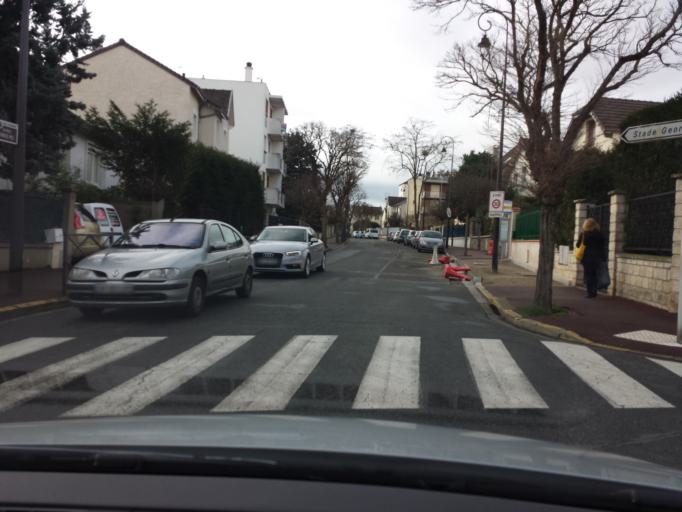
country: FR
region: Ile-de-France
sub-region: Departement des Hauts-de-Seine
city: Antony
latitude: 48.7513
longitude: 2.2898
